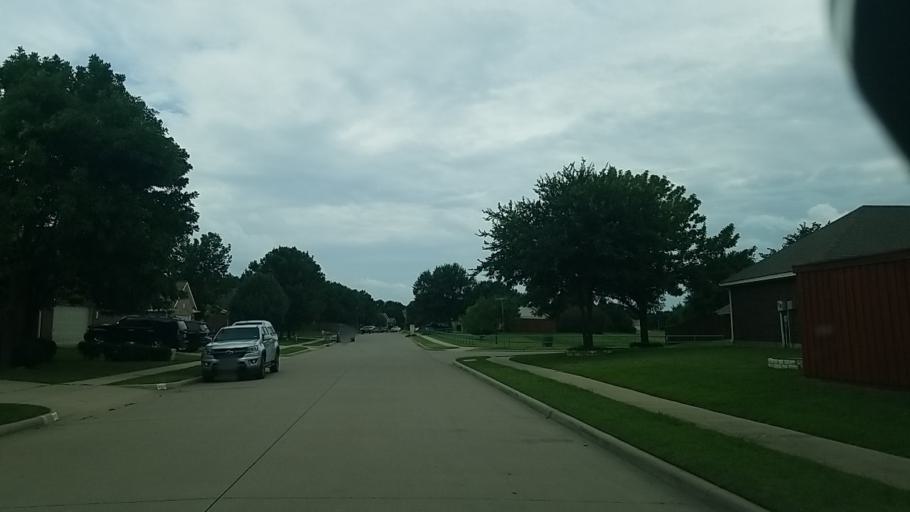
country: US
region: Texas
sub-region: Denton County
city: Corinth
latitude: 33.1695
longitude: -97.1070
